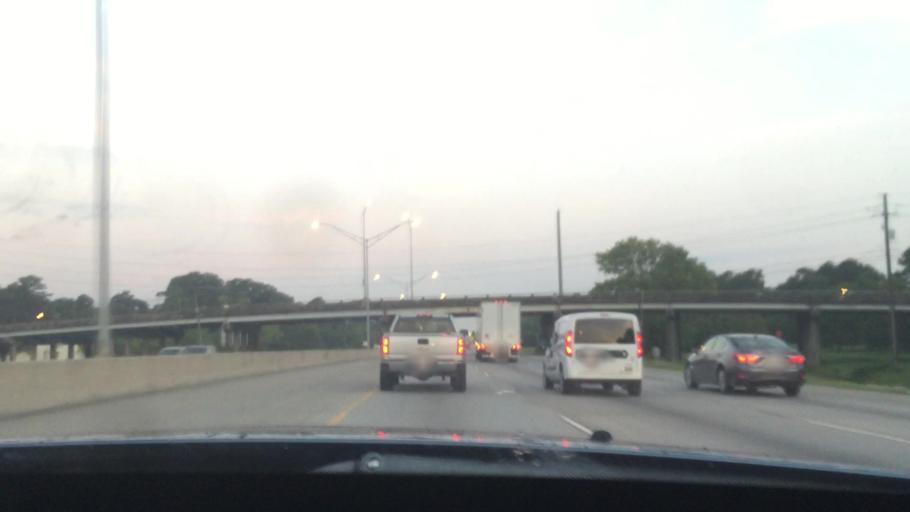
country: US
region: Louisiana
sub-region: East Baton Rouge Parish
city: Westminster
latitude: 30.4171
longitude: -91.0965
